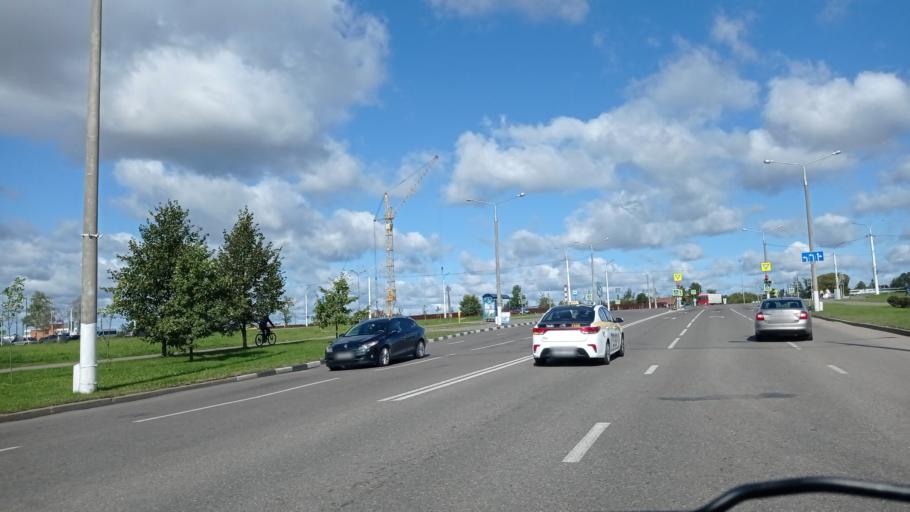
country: BY
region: Vitebsk
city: Vitebsk
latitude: 55.1729
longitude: 30.2583
